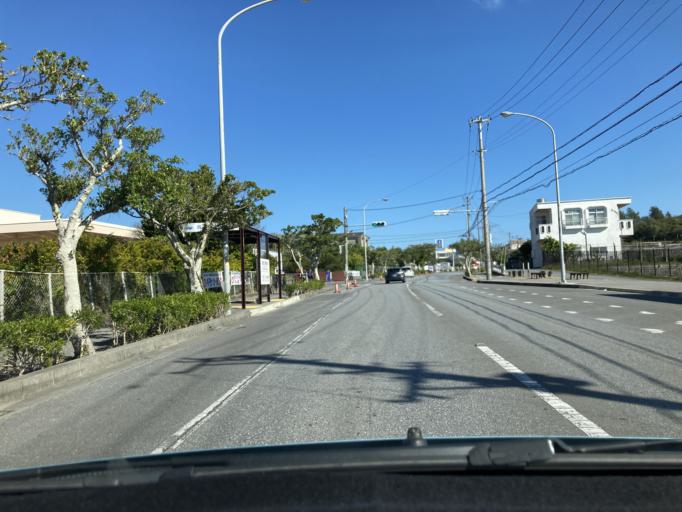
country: JP
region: Okinawa
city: Gushikawa
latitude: 26.3533
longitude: 127.8449
